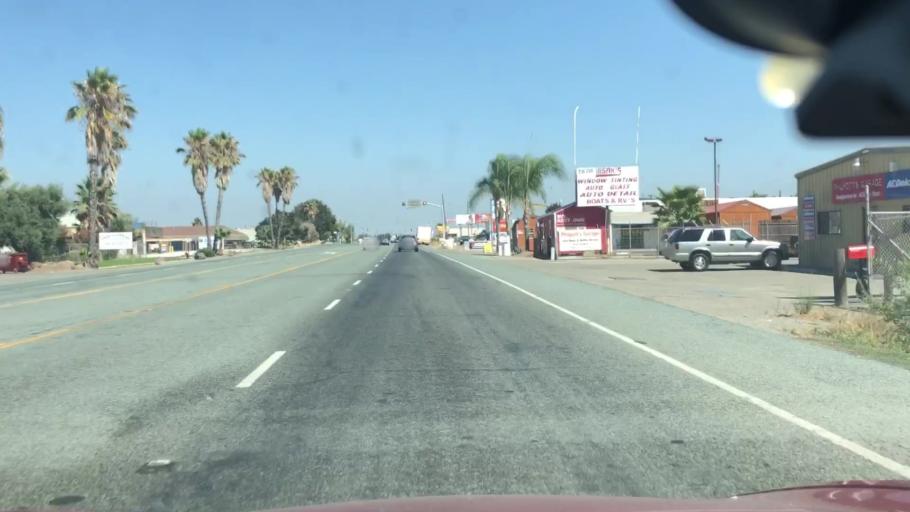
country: US
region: California
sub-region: San Joaquin County
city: Tracy
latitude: 37.7403
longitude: -121.4032
